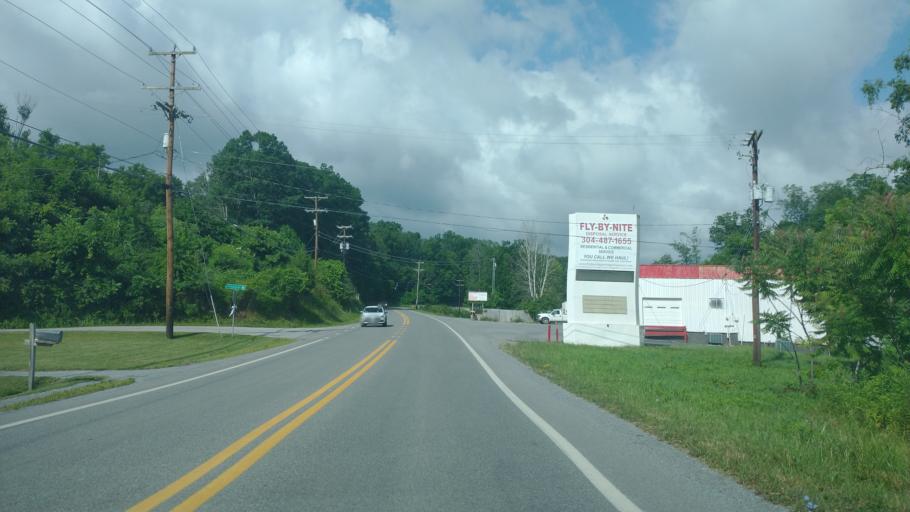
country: US
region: West Virginia
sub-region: Mercer County
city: Princeton
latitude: 37.3615
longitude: -81.1272
